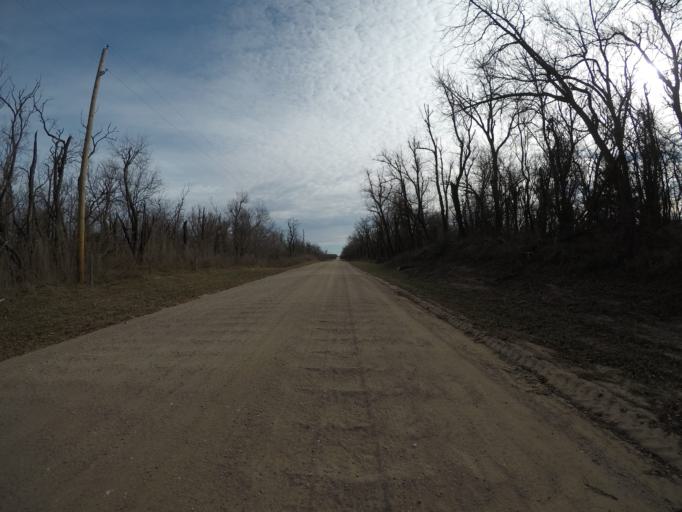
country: US
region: Kansas
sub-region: Reno County
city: Hutchinson
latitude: 38.1010
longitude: -97.8586
